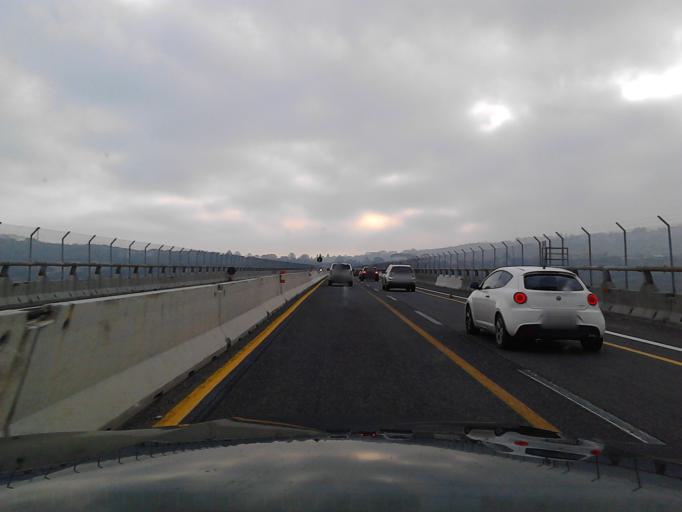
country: IT
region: Abruzzo
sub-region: Provincia di Teramo
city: Salino
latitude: 42.7783
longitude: 13.9329
